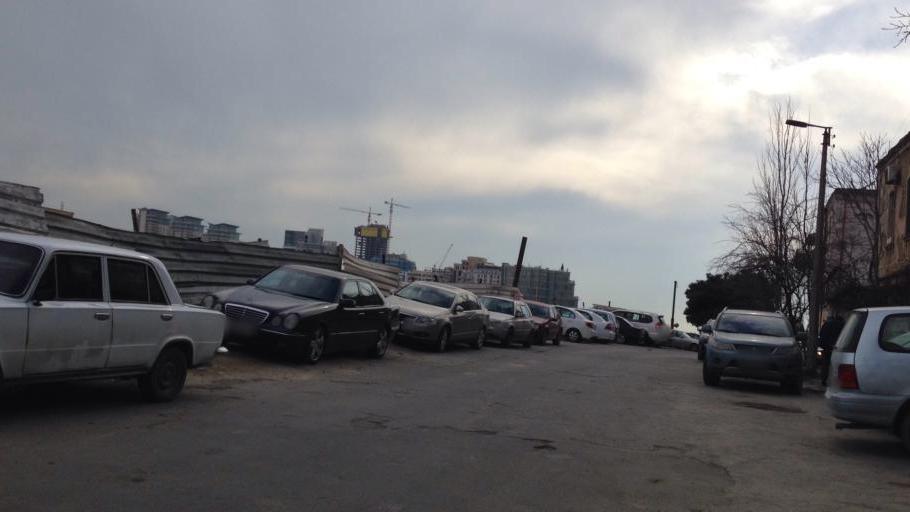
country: AZ
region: Baki
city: Baku
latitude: 40.3828
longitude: 49.8497
